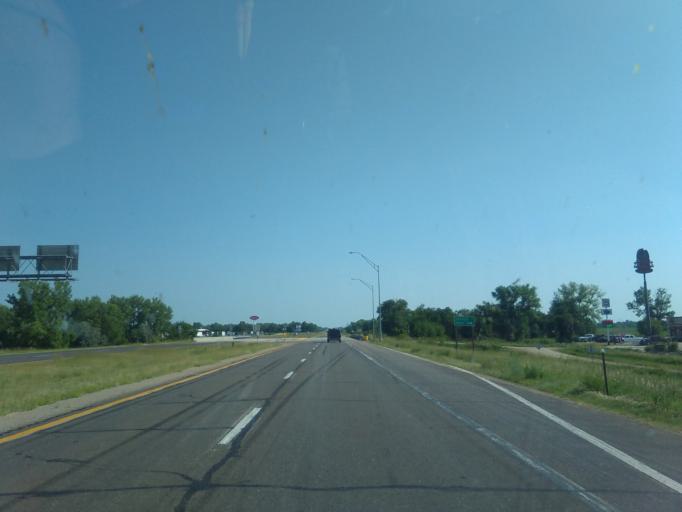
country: US
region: Nebraska
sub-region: Hall County
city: Grand Island
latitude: 40.8167
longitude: -98.3785
